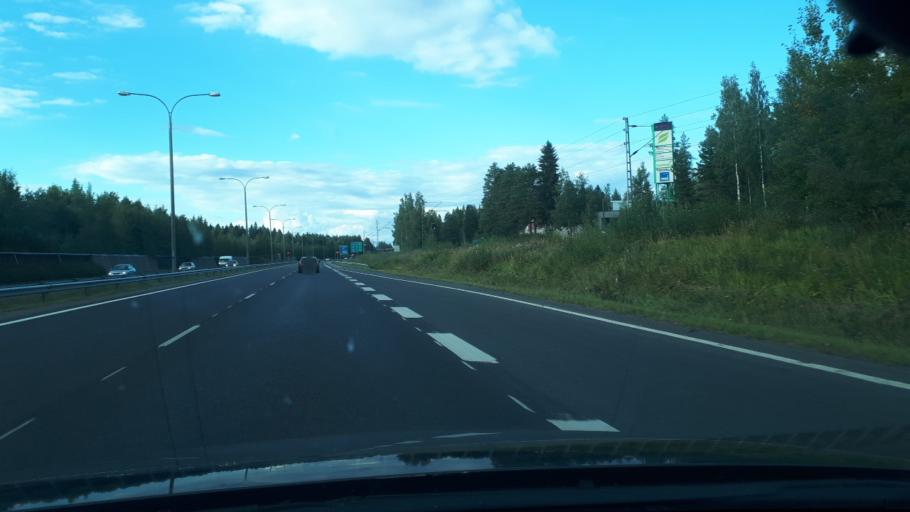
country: FI
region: Northern Savo
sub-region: Kuopio
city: Kuopio
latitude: 62.9776
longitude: 27.7059
